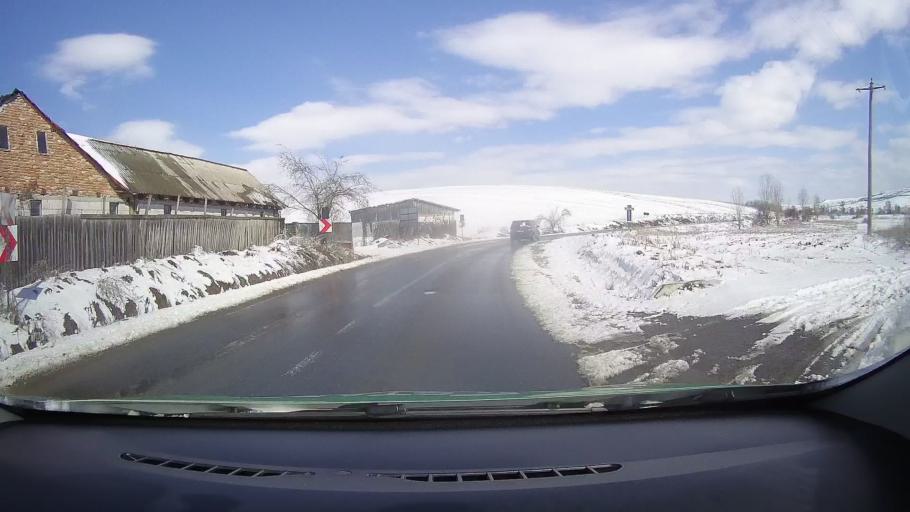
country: RO
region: Sibiu
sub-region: Comuna Nocrich
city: Nocrich
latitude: 45.9016
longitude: 24.4595
